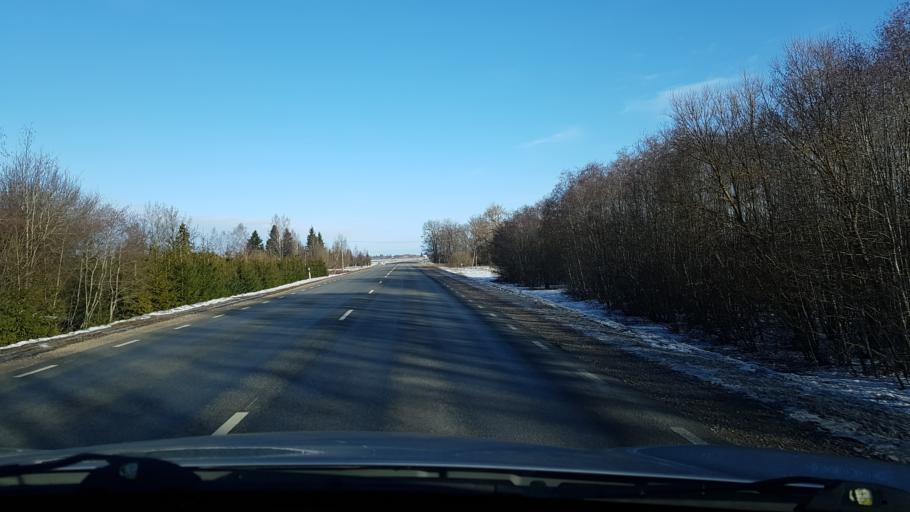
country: EE
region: Viljandimaa
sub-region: Vohma linn
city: Vohma
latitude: 58.6373
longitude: 25.5749
